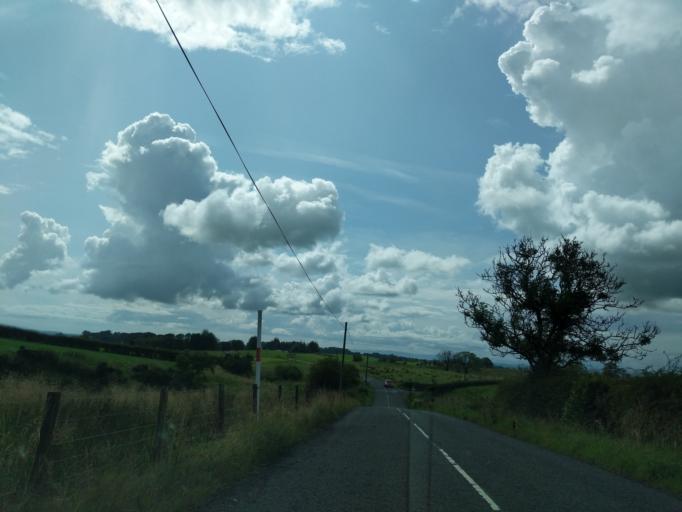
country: GB
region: Scotland
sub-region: East Ayrshire
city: Stewarton
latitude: 55.7252
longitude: -4.4850
